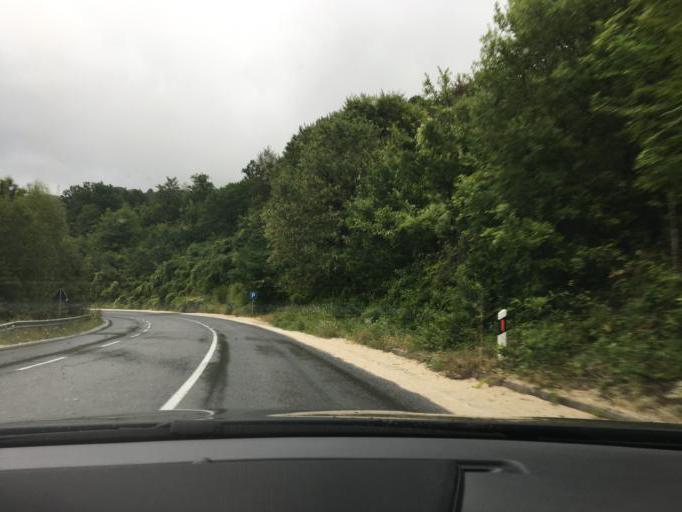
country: MK
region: Kriva Palanka
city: Kriva Palanka
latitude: 42.2200
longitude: 22.4461
